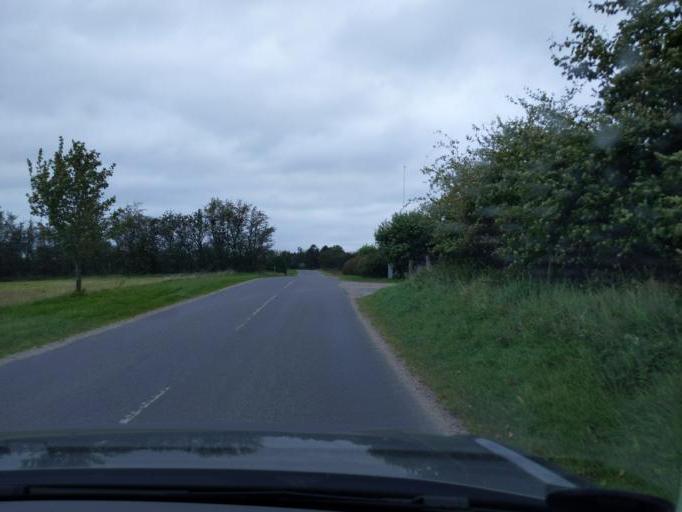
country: DK
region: Central Jutland
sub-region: Viborg Kommune
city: Bjerringbro
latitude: 56.5394
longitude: 9.6100
